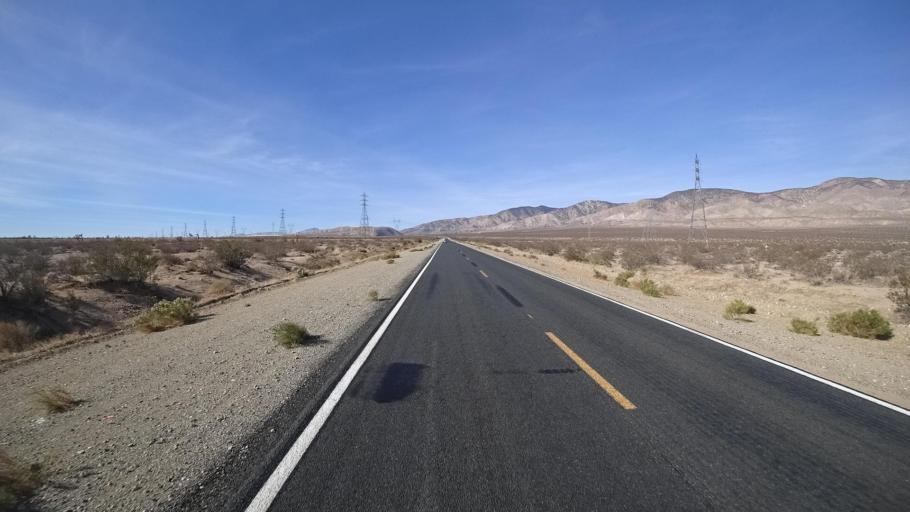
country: US
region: California
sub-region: Kern County
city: Mojave
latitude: 35.1255
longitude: -118.1573
